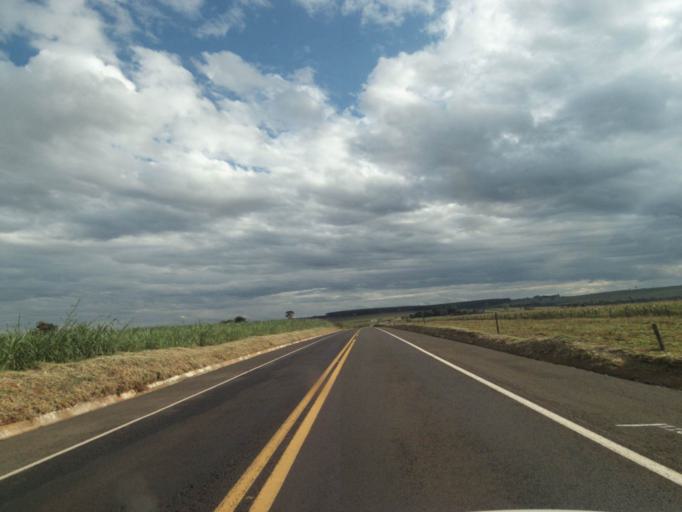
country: PY
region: Canindeyu
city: Salto del Guaira
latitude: -24.0804
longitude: -54.0639
